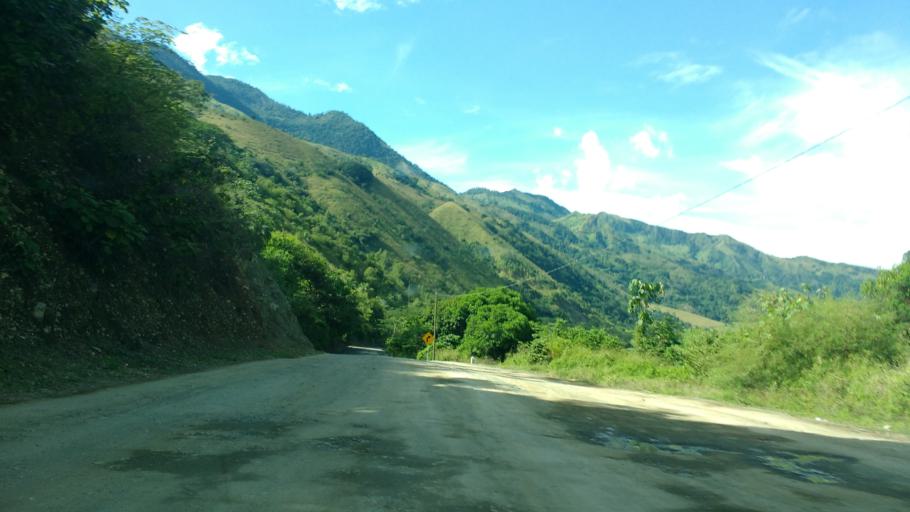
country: CO
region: Antioquia
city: Concordia
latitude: 6.0408
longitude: -75.8619
